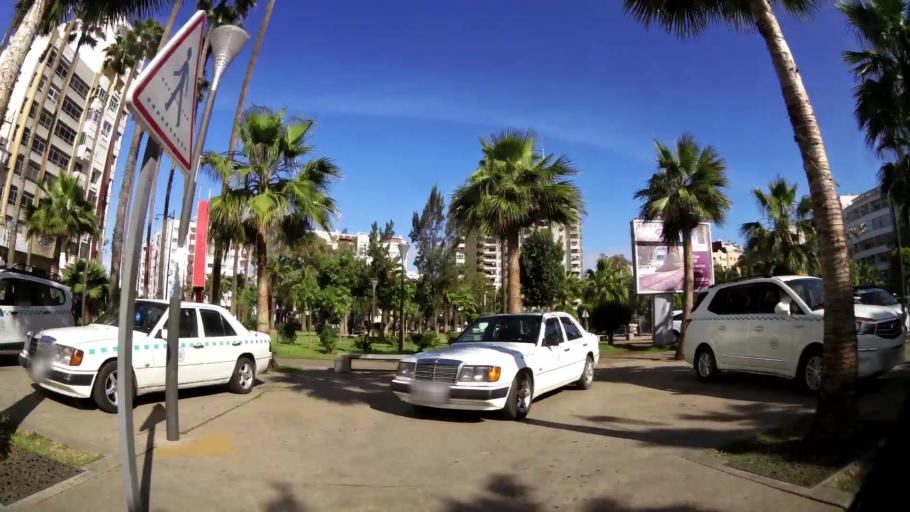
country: MA
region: Grand Casablanca
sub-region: Casablanca
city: Casablanca
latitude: 33.5898
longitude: -7.5917
